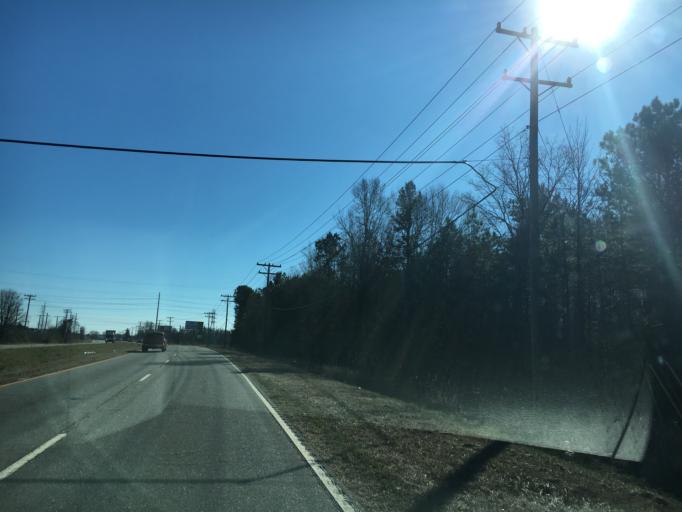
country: US
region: South Carolina
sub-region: Anderson County
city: Homeland Park
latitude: 34.4434
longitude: -82.6672
